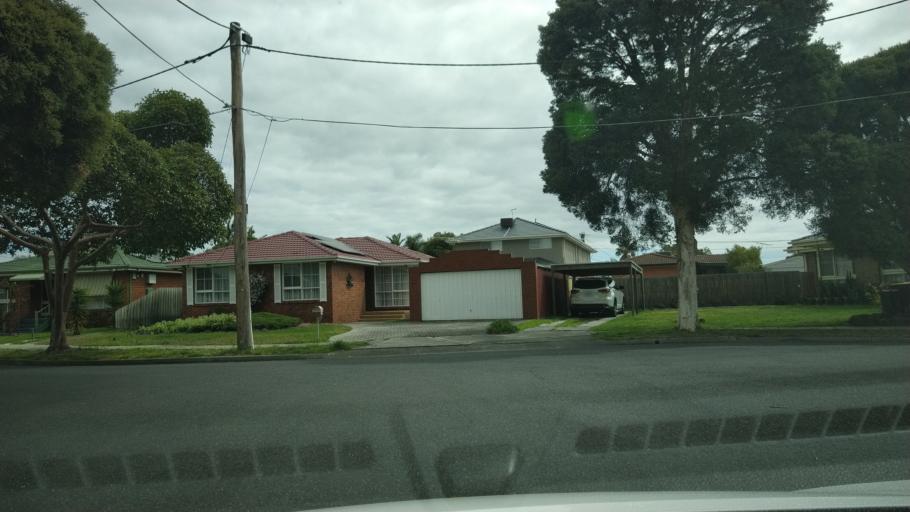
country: AU
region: Victoria
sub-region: Greater Dandenong
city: Noble Park
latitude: -37.9779
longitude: 145.1620
